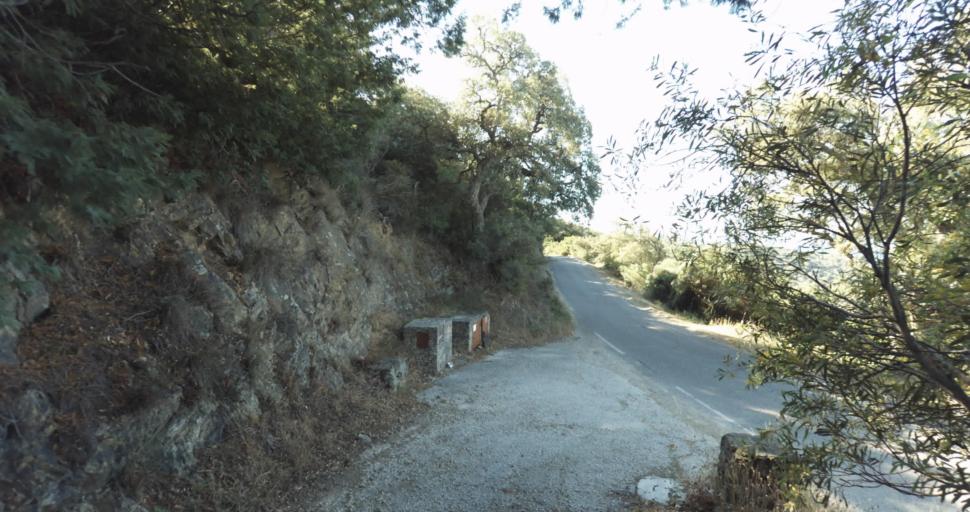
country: FR
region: Provence-Alpes-Cote d'Azur
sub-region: Departement du Var
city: Ramatuelle
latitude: 43.2172
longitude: 6.6005
